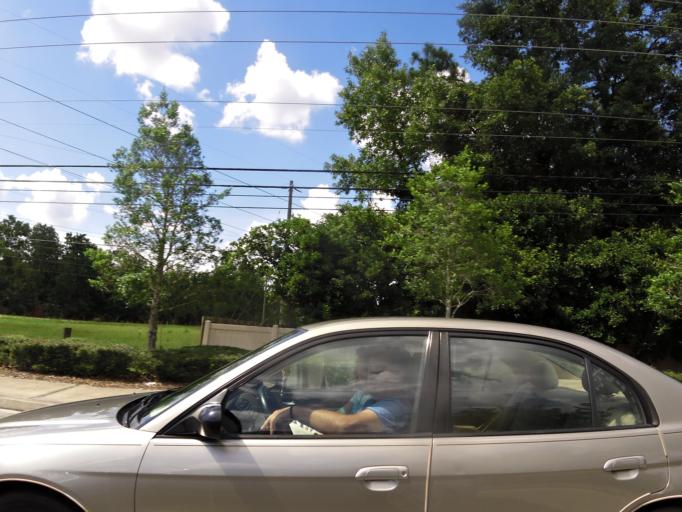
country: US
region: Florida
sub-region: Saint Johns County
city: Fruit Cove
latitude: 30.1412
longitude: -81.5347
